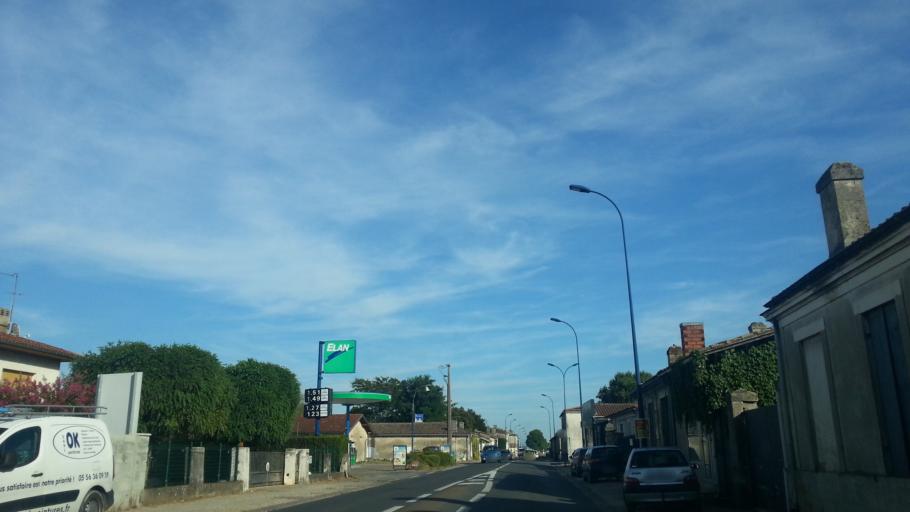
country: FR
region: Aquitaine
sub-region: Departement de la Gironde
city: Portets
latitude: 44.6881
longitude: -0.4174
